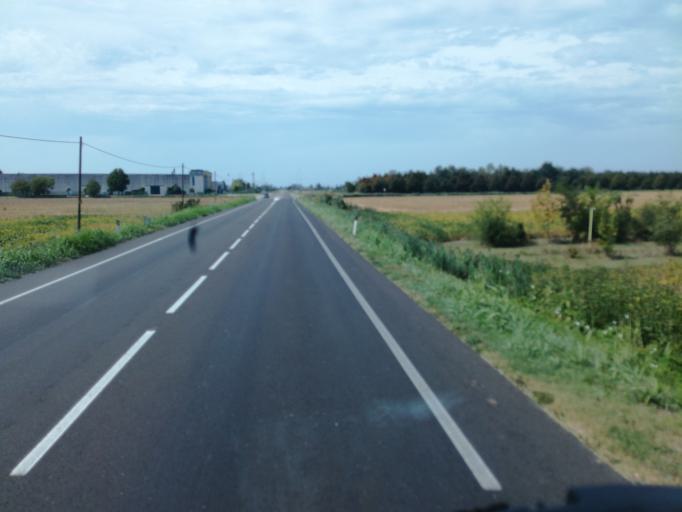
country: IT
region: Veneto
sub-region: Provincia di Padova
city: Candiana
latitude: 45.2129
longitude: 11.9804
